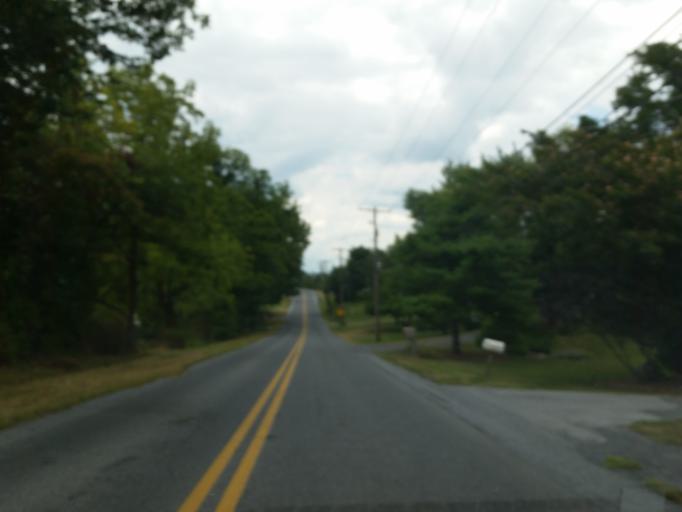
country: US
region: Pennsylvania
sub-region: Lebanon County
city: Palmyra
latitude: 40.3875
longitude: -76.6300
